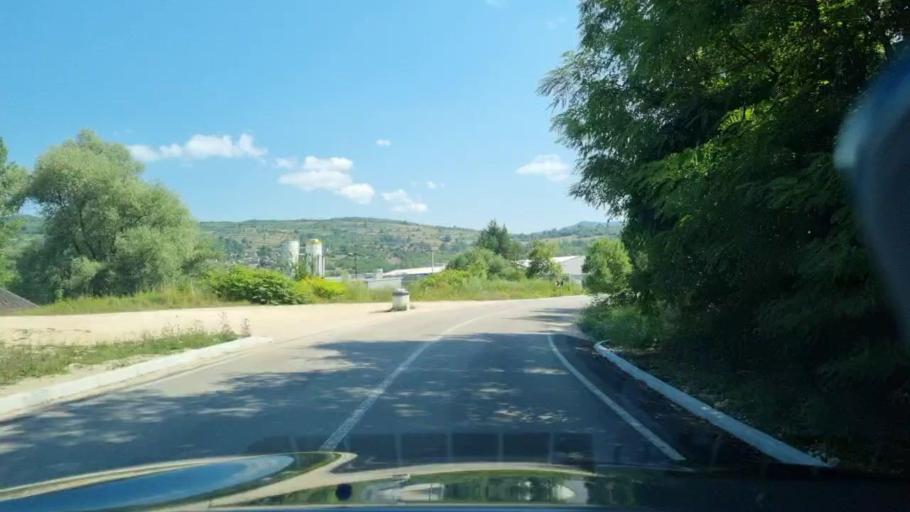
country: BA
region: Federation of Bosnia and Herzegovina
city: Kljuc
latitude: 44.5533
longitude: 16.7897
